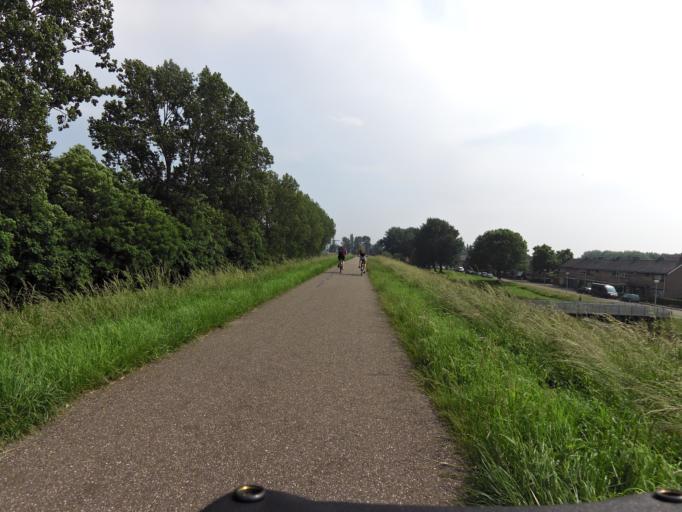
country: NL
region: South Holland
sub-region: Gemeente Spijkenisse
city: Spijkenisse
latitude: 51.8579
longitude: 4.3267
